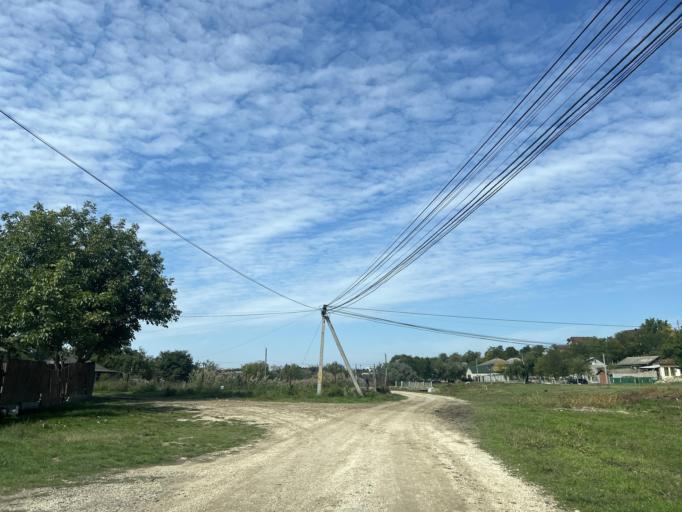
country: MD
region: Ungheni
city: Ungheni
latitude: 47.1966
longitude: 27.8118
